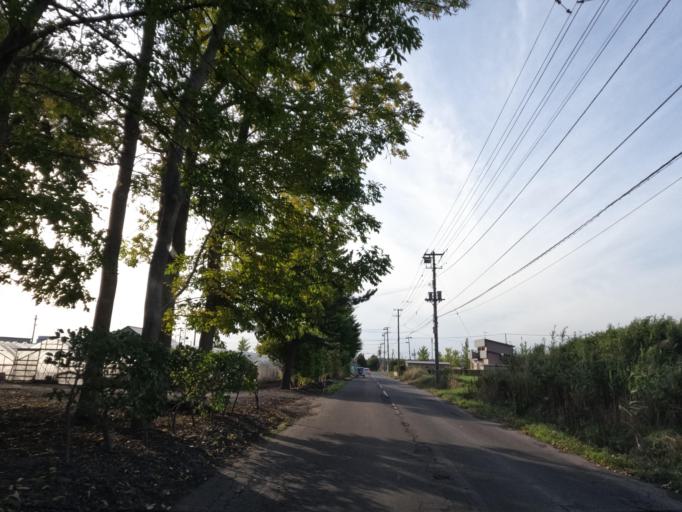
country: JP
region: Hokkaido
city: Date
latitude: 42.4755
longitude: 140.8861
